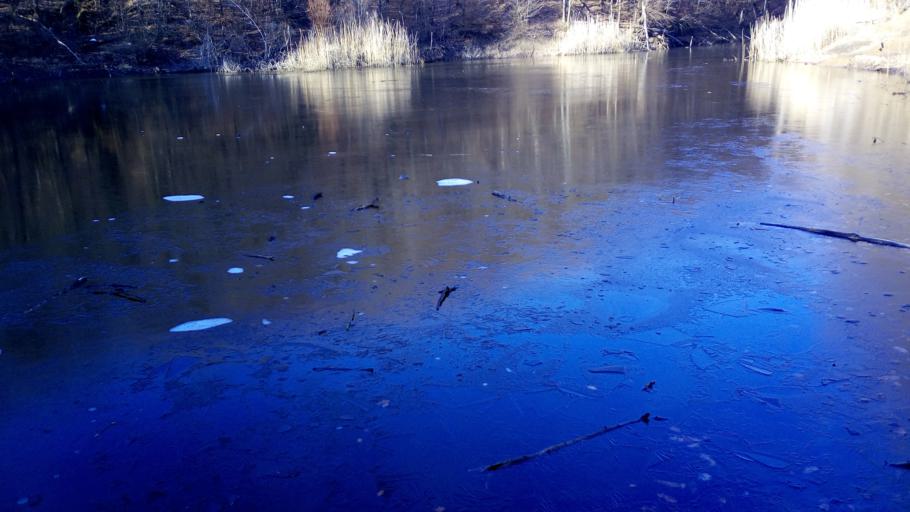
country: HU
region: Baranya
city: Pecs
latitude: 46.1145
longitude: 18.2382
